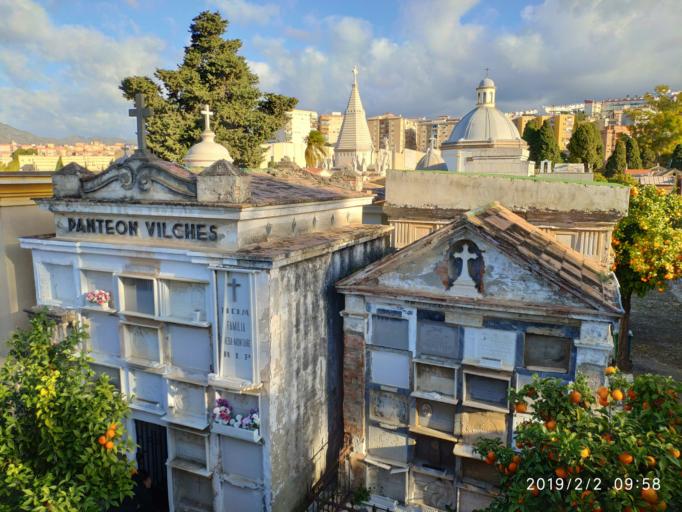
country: ES
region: Andalusia
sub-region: Provincia de Malaga
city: Malaga
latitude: 36.7334
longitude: -4.4183
